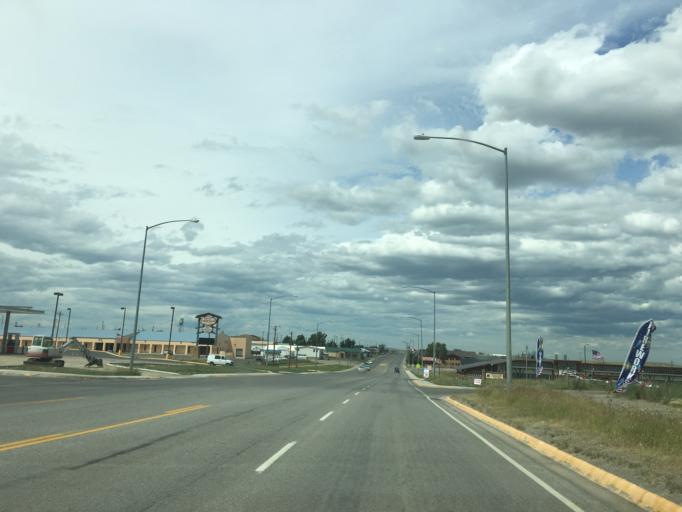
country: US
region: Montana
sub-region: Glacier County
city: South Browning
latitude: 48.5484
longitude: -113.0097
